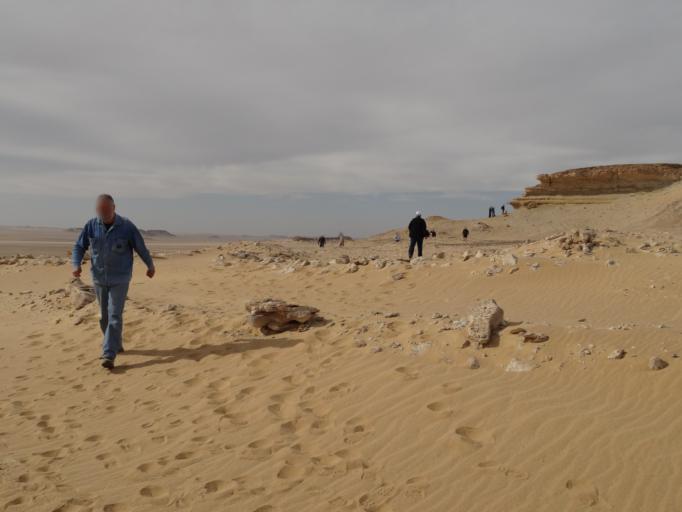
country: EG
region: Al Jizah
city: Al Bawiti
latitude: 28.7775
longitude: 29.2479
